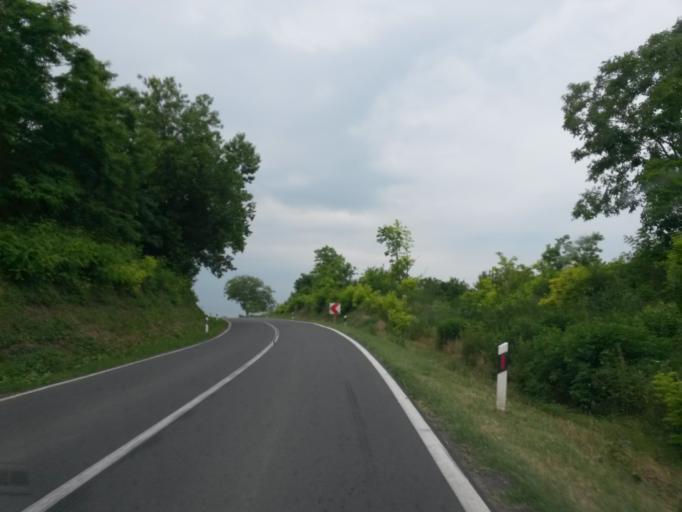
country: HR
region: Vukovarsko-Srijemska
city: Bapska
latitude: 45.2356
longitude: 19.2549
